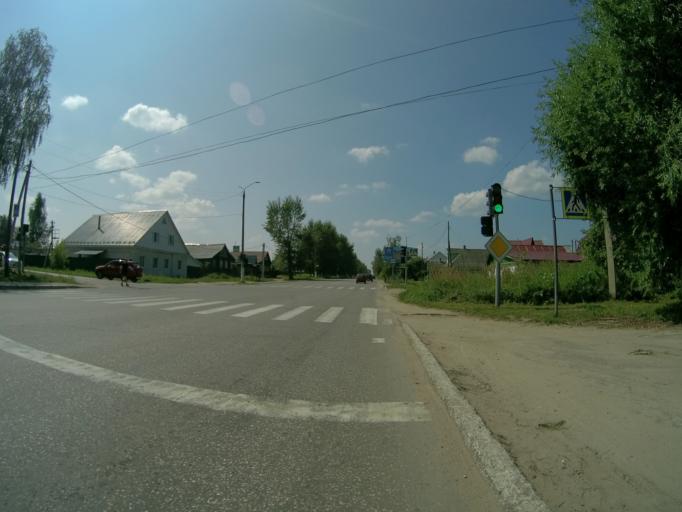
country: RU
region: Vladimir
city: Gus'-Khrustal'nyy
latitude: 55.6270
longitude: 40.6864
